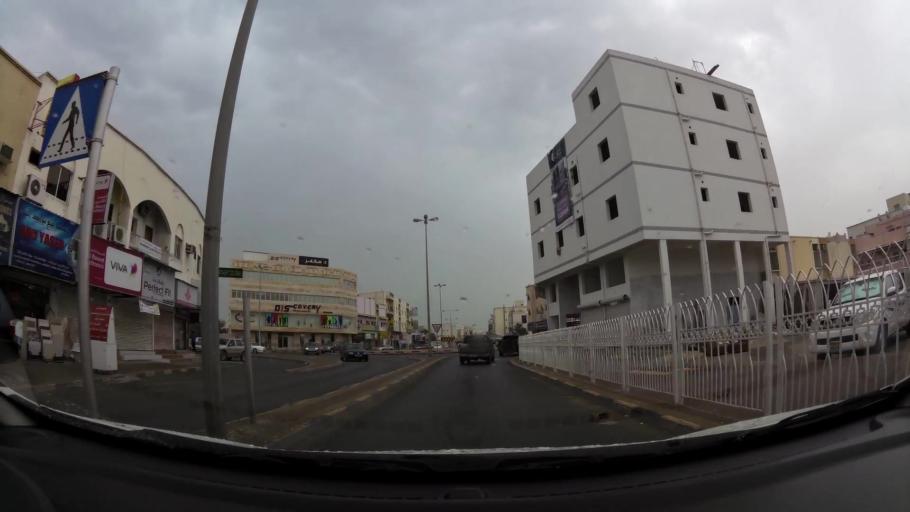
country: BH
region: Northern
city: Madinat `Isa
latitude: 26.1703
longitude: 50.5646
